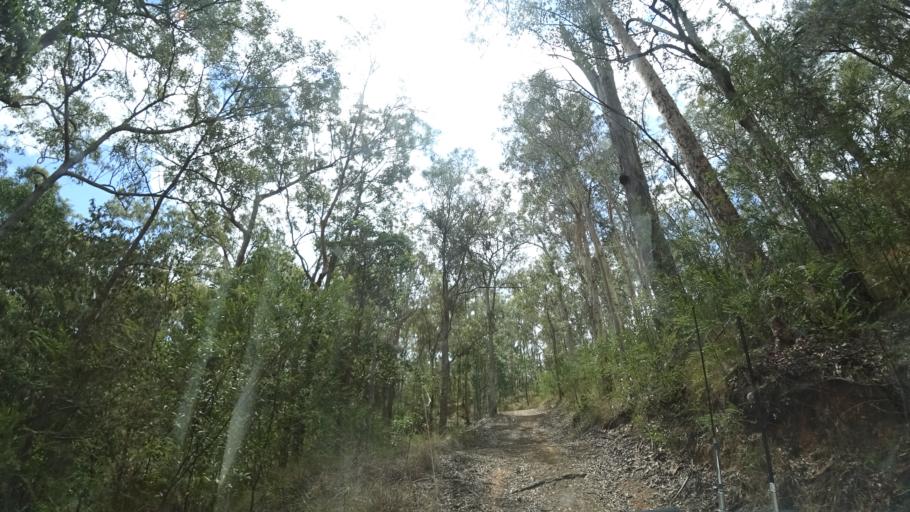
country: AU
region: Queensland
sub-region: Moreton Bay
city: Highvale
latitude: -27.4061
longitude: 152.7408
